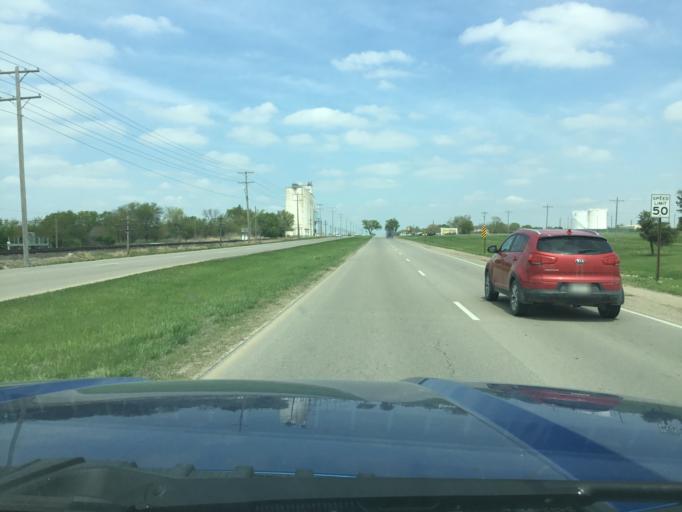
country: US
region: Kansas
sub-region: Shawnee County
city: Topeka
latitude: 38.9540
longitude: -95.6872
